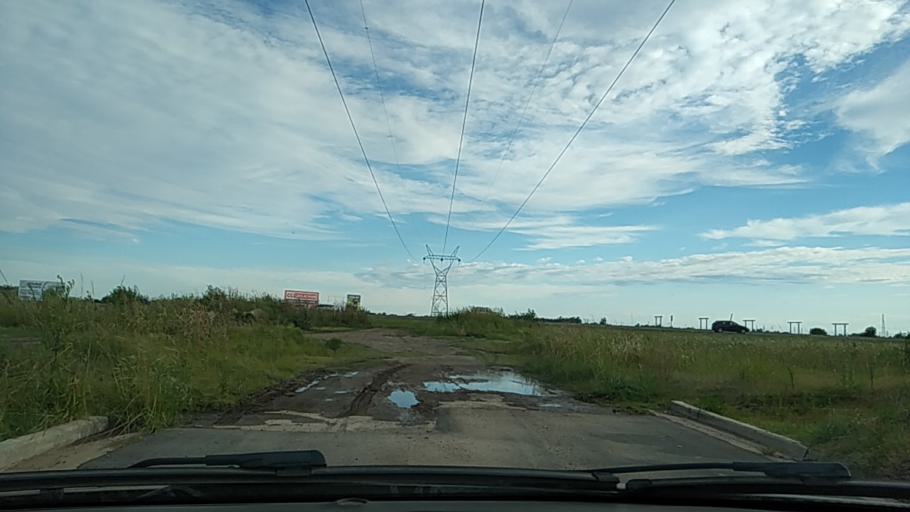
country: AR
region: Santa Fe
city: Perez
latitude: -32.9474
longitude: -60.7639
